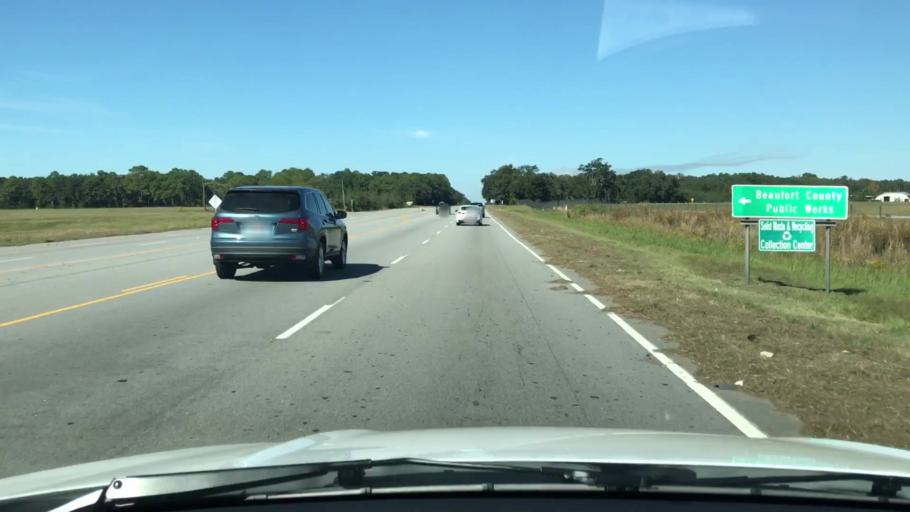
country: US
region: South Carolina
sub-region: Beaufort County
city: Burton
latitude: 32.4656
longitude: -80.7354
